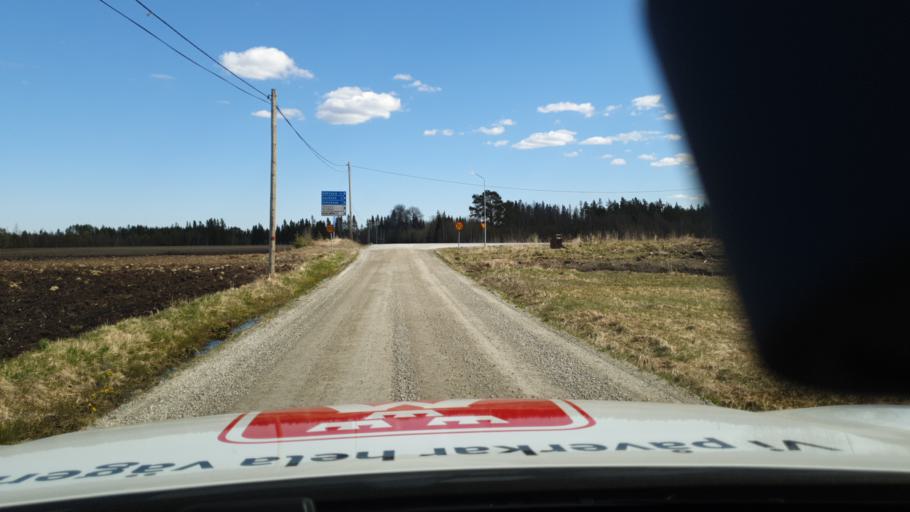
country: SE
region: Jaemtland
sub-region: Bergs Kommun
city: Hoverberg
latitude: 62.9162
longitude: 14.3167
